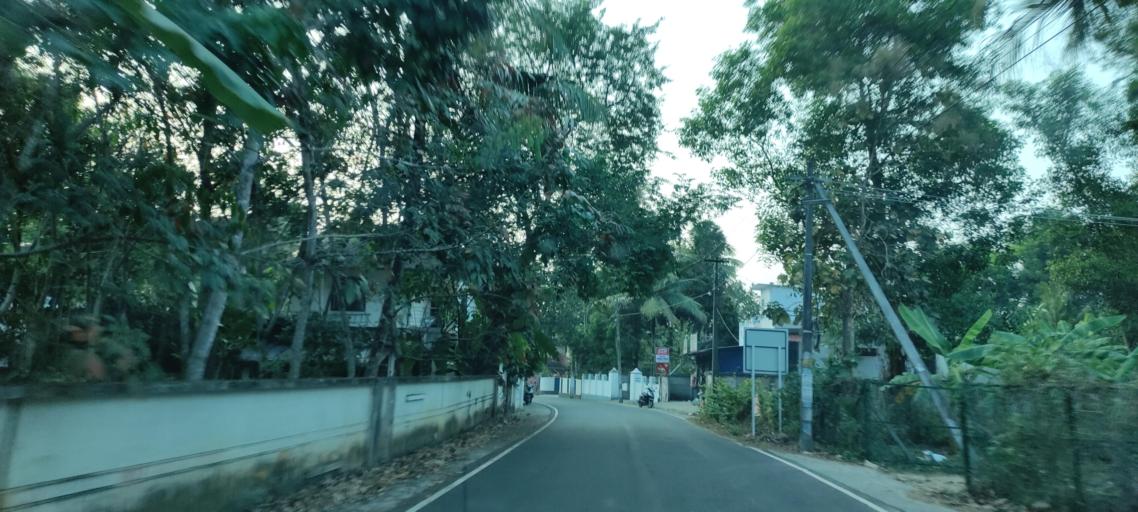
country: IN
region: Kerala
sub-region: Alappuzha
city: Mavelikara
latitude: 9.2775
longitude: 76.5588
